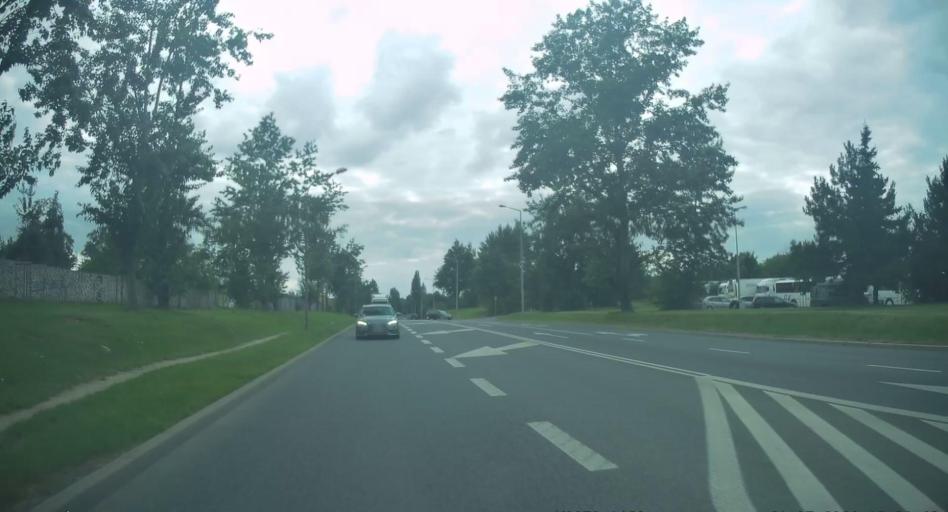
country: PL
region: Lower Silesian Voivodeship
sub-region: Powiat swidnicki
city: Swidnica
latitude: 50.8532
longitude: 16.4959
